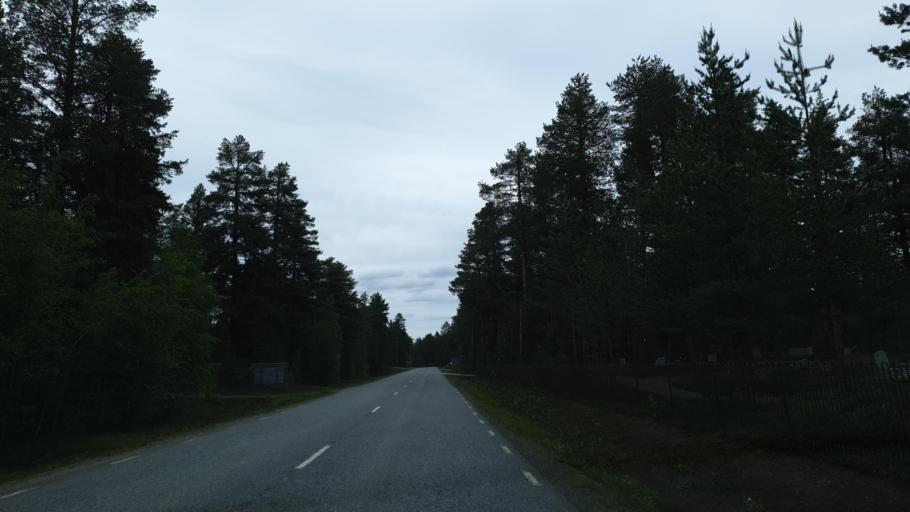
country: SE
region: Vaesterbotten
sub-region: Sorsele Kommun
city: Sorsele
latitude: 65.5472
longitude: 17.5083
